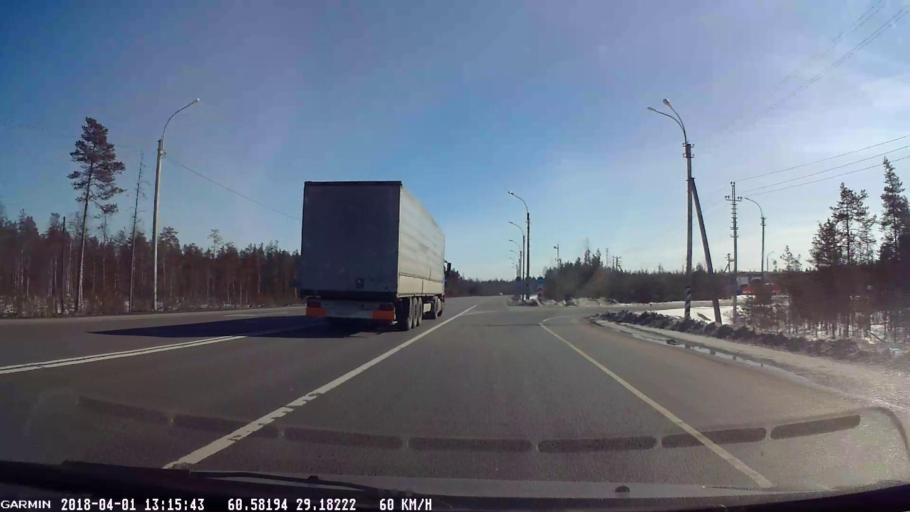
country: RU
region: Leningrad
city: Veshchevo
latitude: 60.5818
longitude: 29.1825
